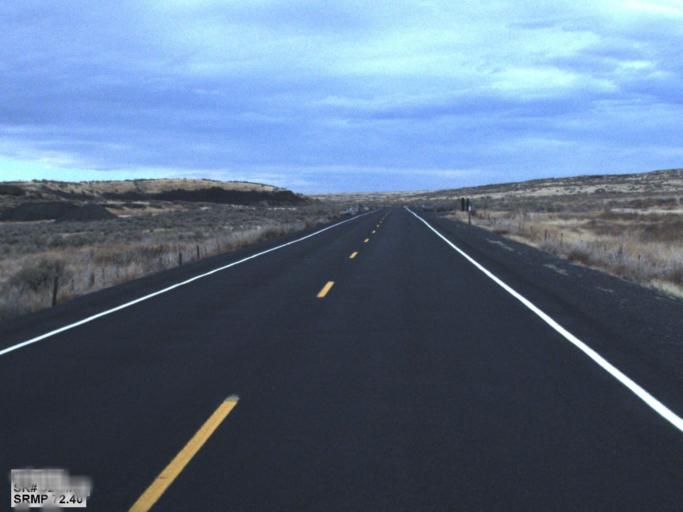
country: US
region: Washington
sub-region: Okanogan County
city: Coulee Dam
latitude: 47.5298
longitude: -118.7827
